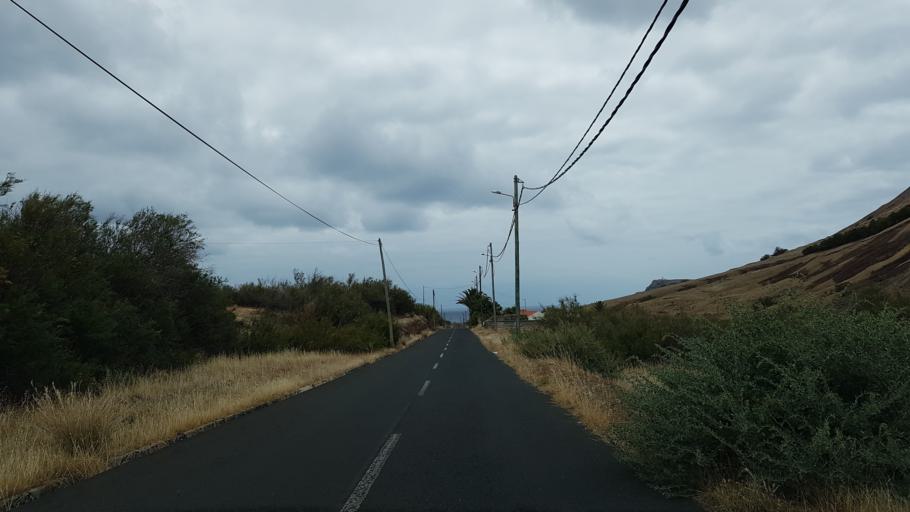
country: PT
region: Madeira
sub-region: Porto Santo
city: Vila de Porto Santo
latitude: 33.0720
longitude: -16.3046
